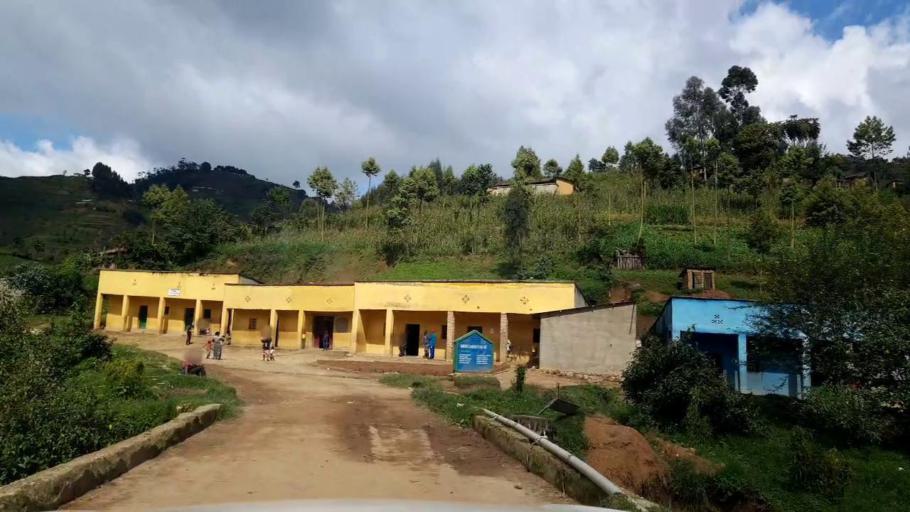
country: RW
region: Western Province
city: Kibuye
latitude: -1.8882
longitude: 29.4665
